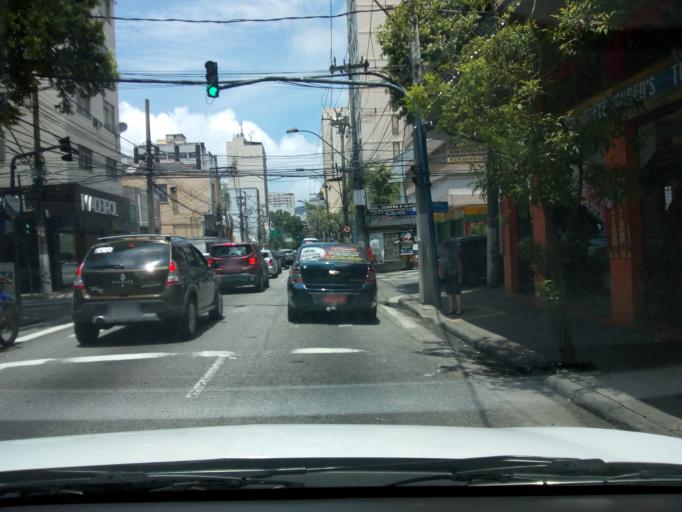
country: BR
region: Rio de Janeiro
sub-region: Niteroi
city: Niteroi
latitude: -22.9028
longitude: -43.1115
